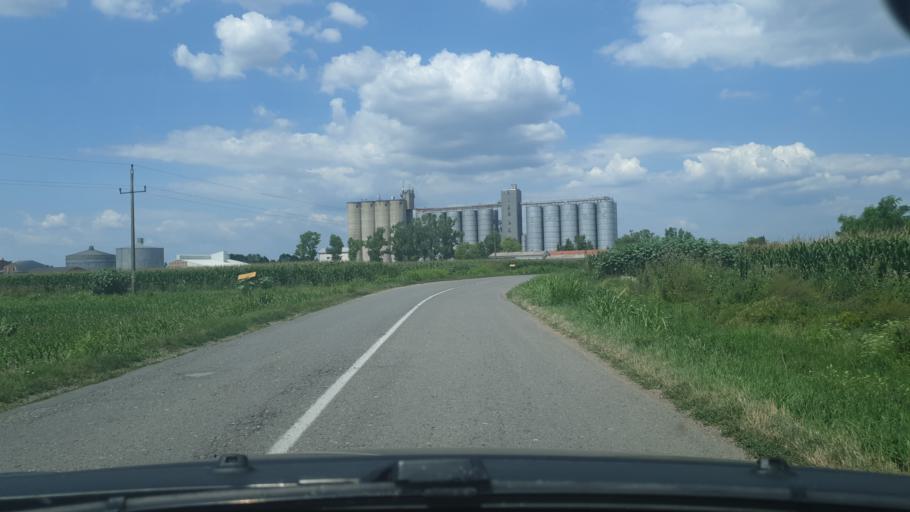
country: RS
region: Autonomna Pokrajina Vojvodina
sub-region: Sremski Okrug
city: Pecinci
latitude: 44.8818
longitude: 19.9603
